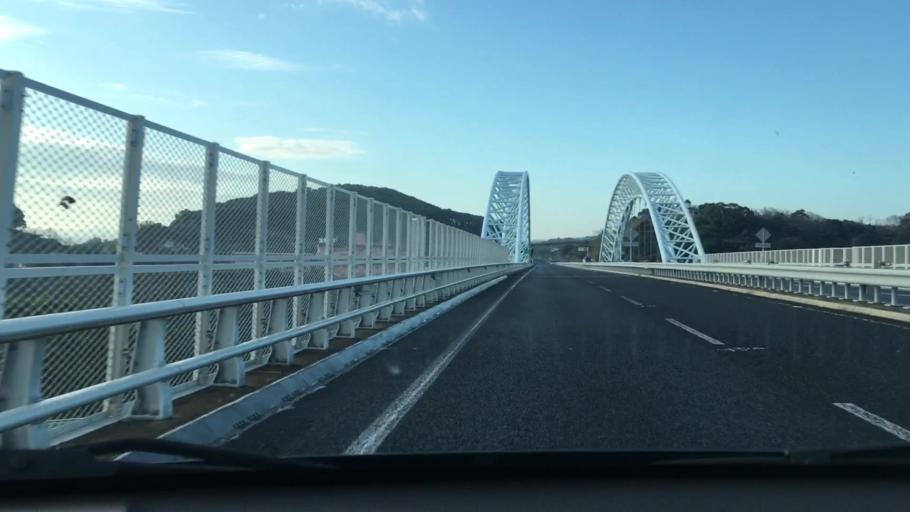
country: JP
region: Nagasaki
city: Sasebo
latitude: 33.0556
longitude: 129.7562
